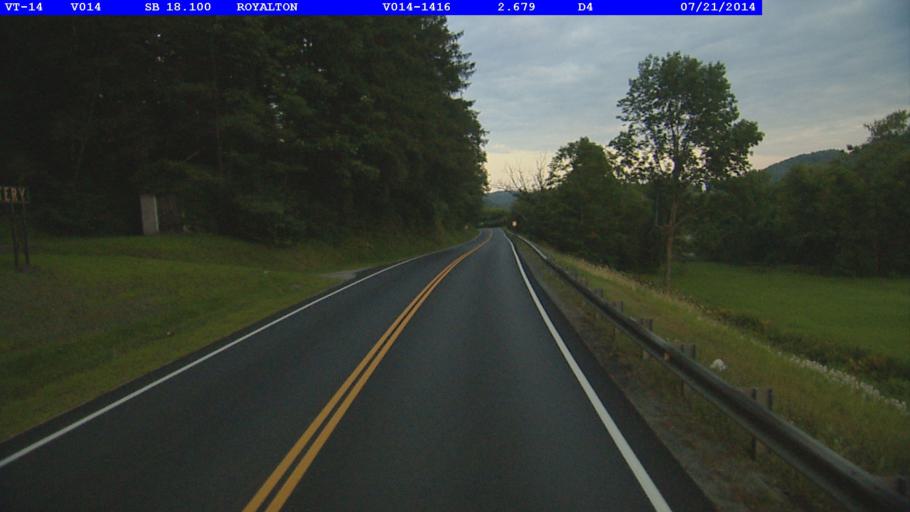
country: US
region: Vermont
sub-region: Orange County
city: Randolph
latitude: 43.8257
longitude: -72.5247
